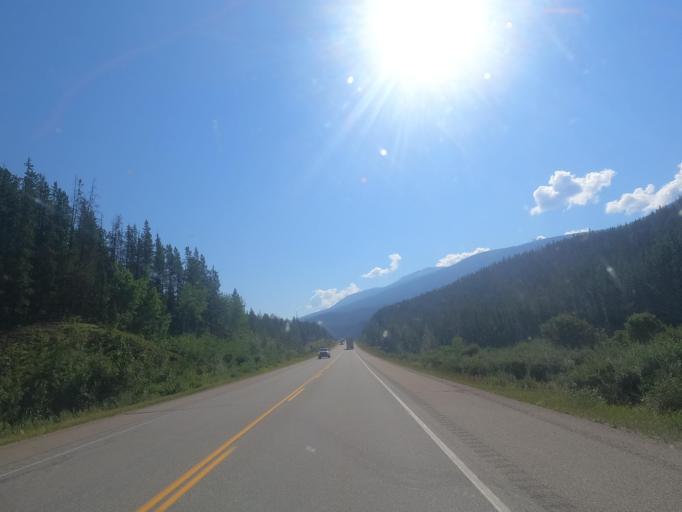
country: CA
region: Alberta
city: Jasper Park Lodge
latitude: 52.8872
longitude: -118.4712
